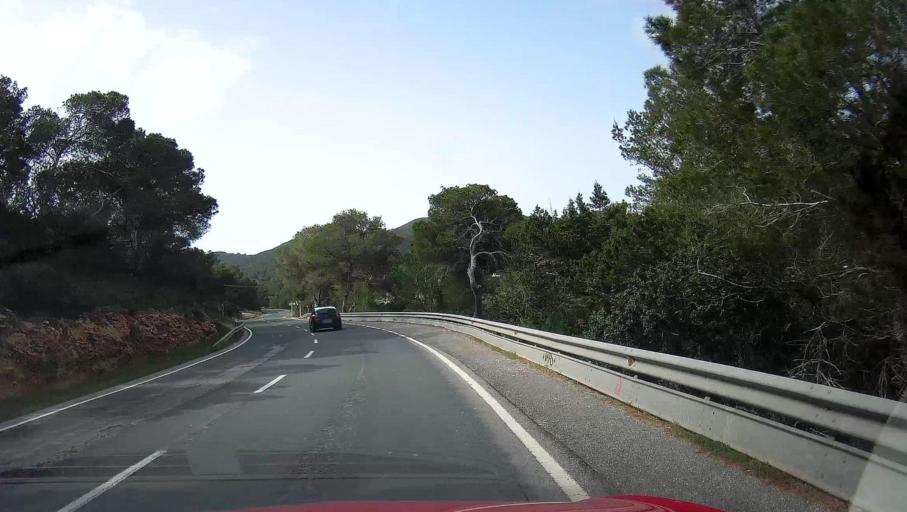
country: ES
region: Balearic Islands
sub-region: Illes Balears
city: Sant Joan de Labritja
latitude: 39.0982
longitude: 1.4987
